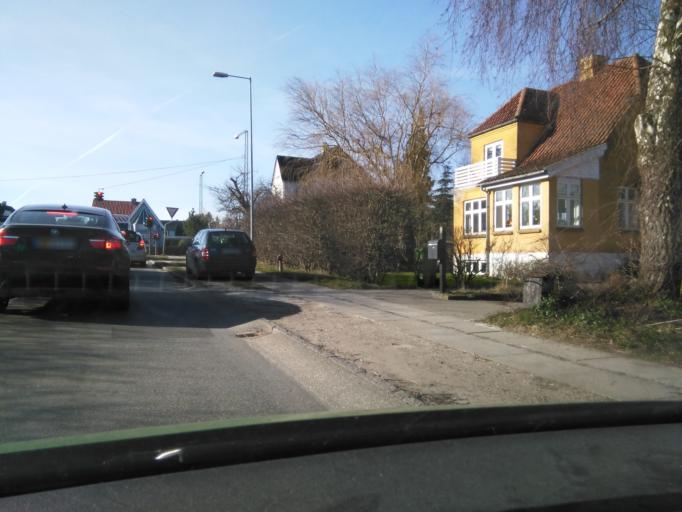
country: DK
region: Central Jutland
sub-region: Arhus Kommune
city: Arhus
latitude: 56.1857
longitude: 10.2191
